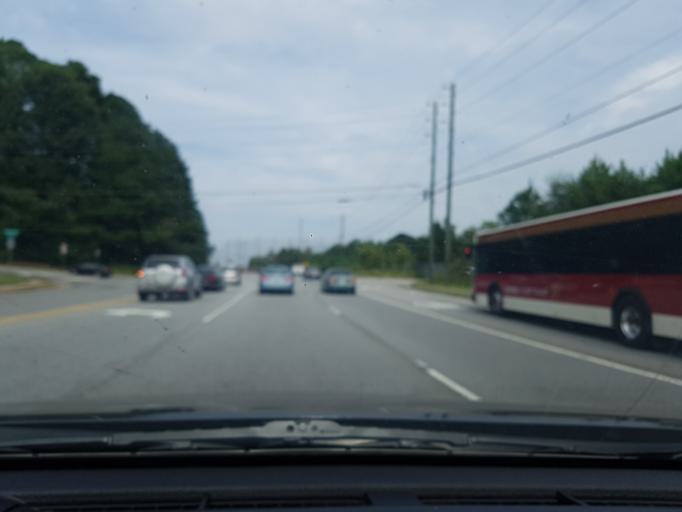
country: US
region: Georgia
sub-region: Gwinnett County
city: Berkeley Lake
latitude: 33.9412
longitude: -84.1640
